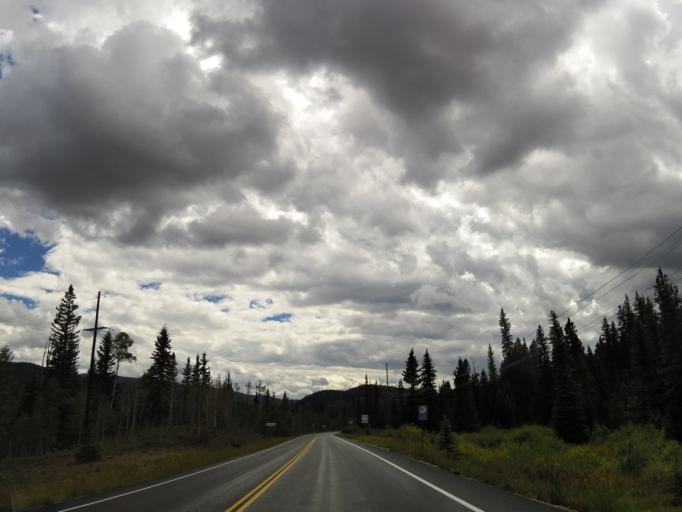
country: US
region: Colorado
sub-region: San Juan County
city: Silverton
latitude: 37.6429
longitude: -107.8069
